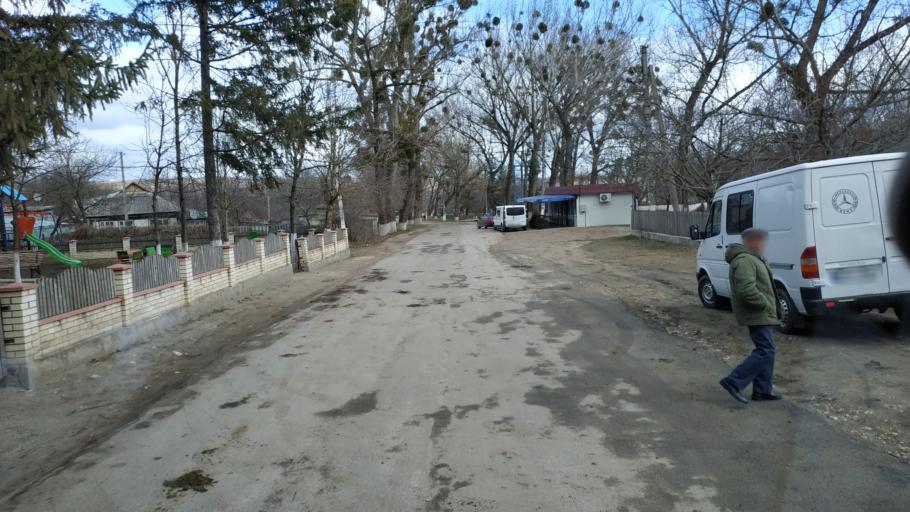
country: MD
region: Calarasi
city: Calarasi
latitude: 47.1264
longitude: 28.3088
